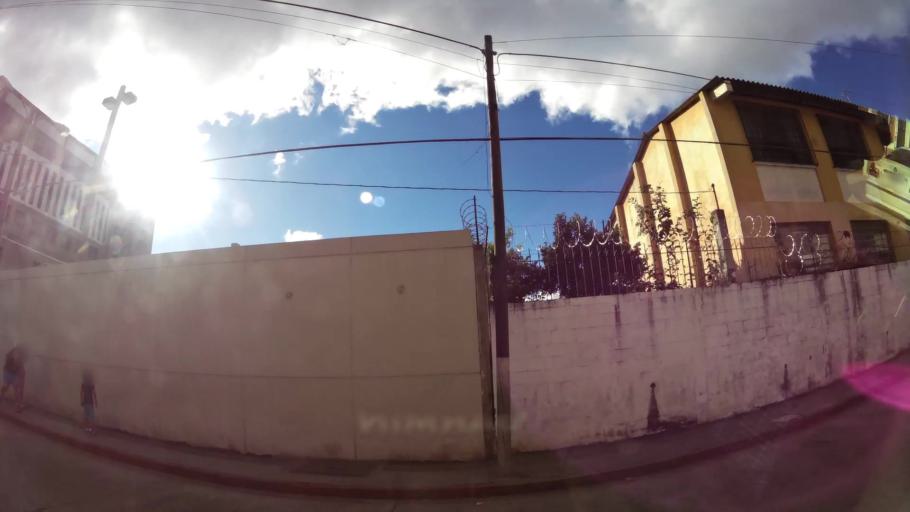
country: GT
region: Guatemala
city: Guatemala City
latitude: 14.6330
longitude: -90.5047
